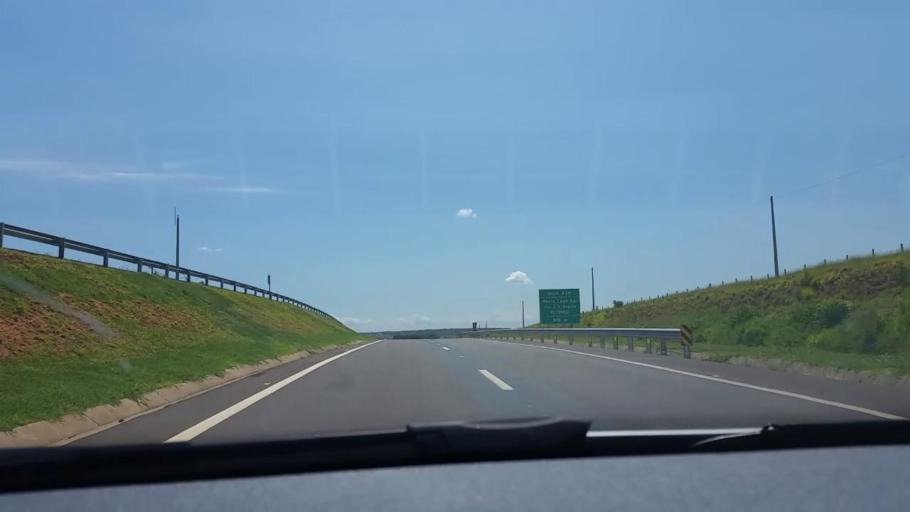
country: BR
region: Sao Paulo
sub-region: Bauru
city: Bauru
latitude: -22.3920
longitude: -49.0795
